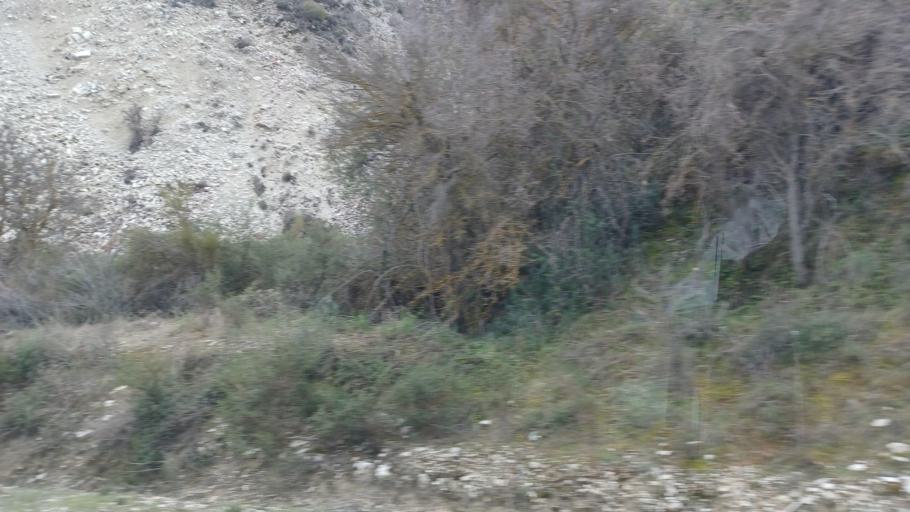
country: CY
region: Limassol
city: Pachna
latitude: 34.8696
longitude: 32.7803
